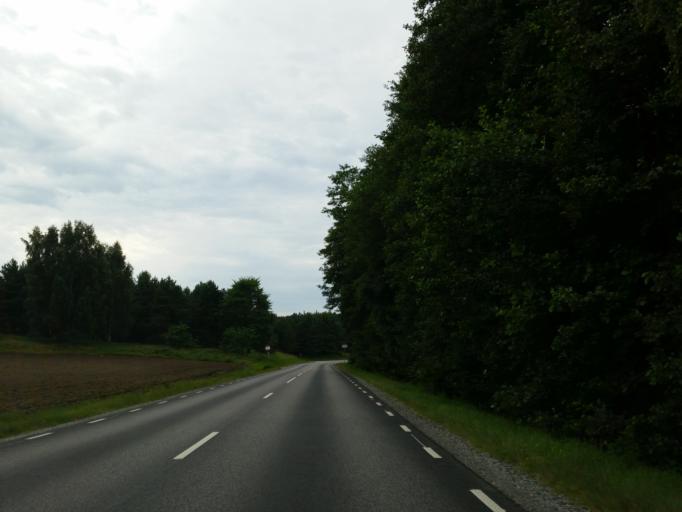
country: SE
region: Stockholm
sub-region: Botkyrka Kommun
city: Eriksberg
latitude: 59.2187
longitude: 17.7796
